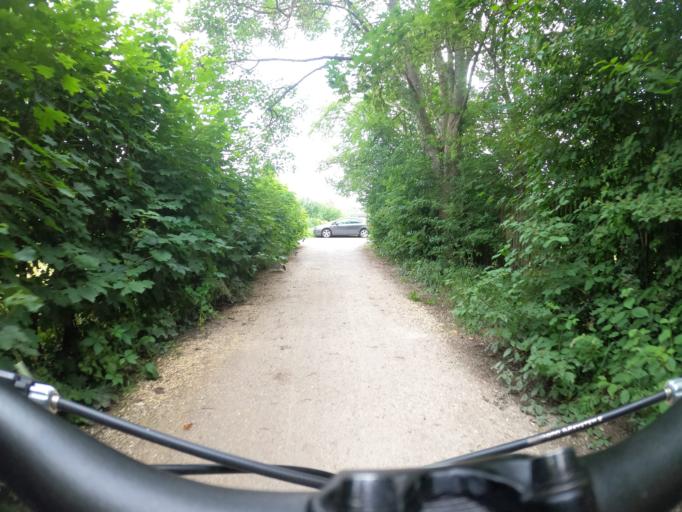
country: DE
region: Bavaria
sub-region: Swabia
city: Neu-Ulm
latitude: 48.4084
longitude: 10.0211
